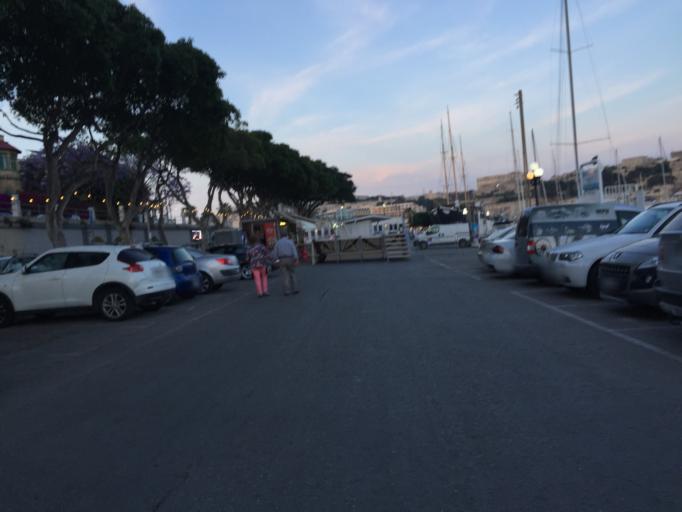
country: MT
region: Ta' Xbiex
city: Ta' Xbiex
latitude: 35.8977
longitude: 14.4982
